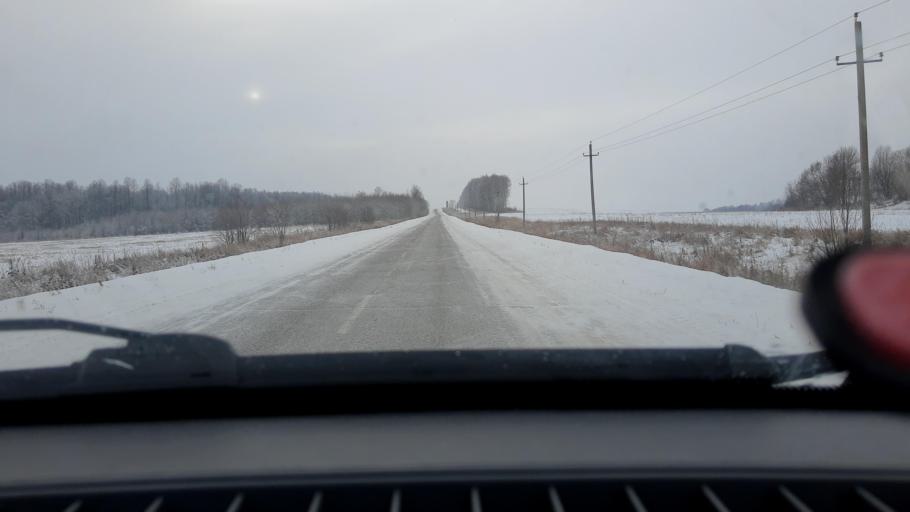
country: RU
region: Bashkortostan
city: Iglino
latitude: 54.6670
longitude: 56.4218
